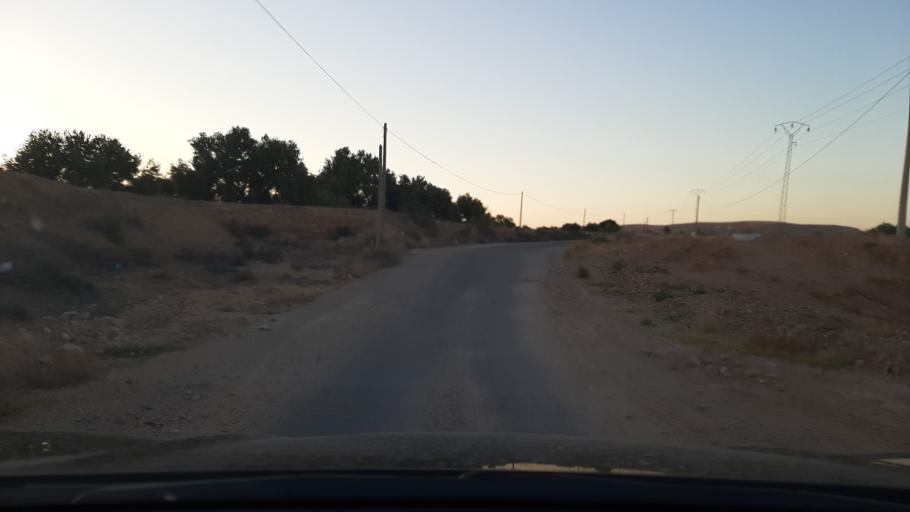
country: TN
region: Qabis
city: Matmata
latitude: 33.5541
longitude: 10.1859
